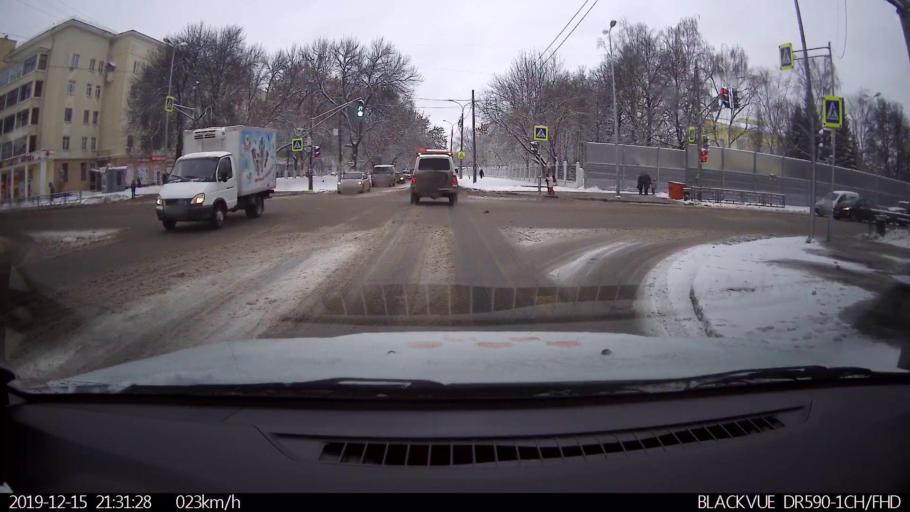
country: RU
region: Nizjnij Novgorod
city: Gorbatovka
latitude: 56.2427
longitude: 43.8497
